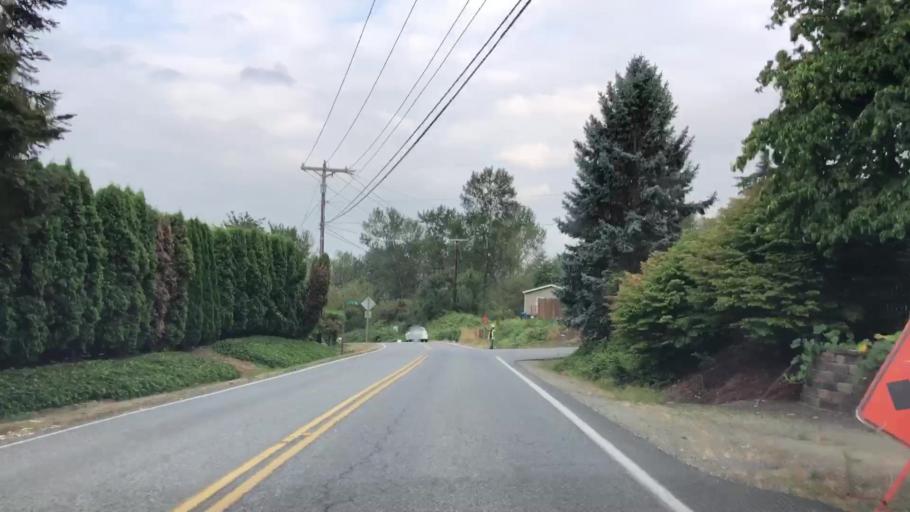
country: US
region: Washington
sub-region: Snohomish County
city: Monroe
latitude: 47.8758
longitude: -121.9885
